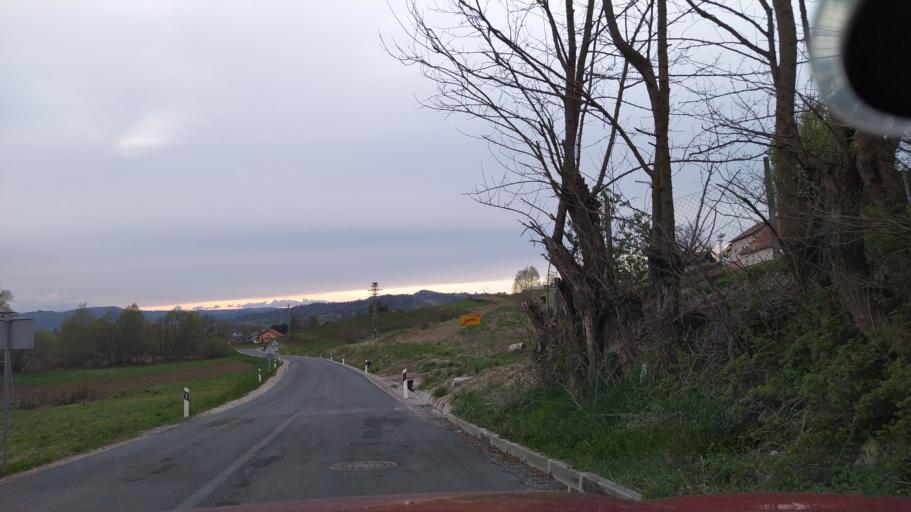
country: HR
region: Varazdinska
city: Jalzabet
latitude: 46.2099
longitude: 16.4808
